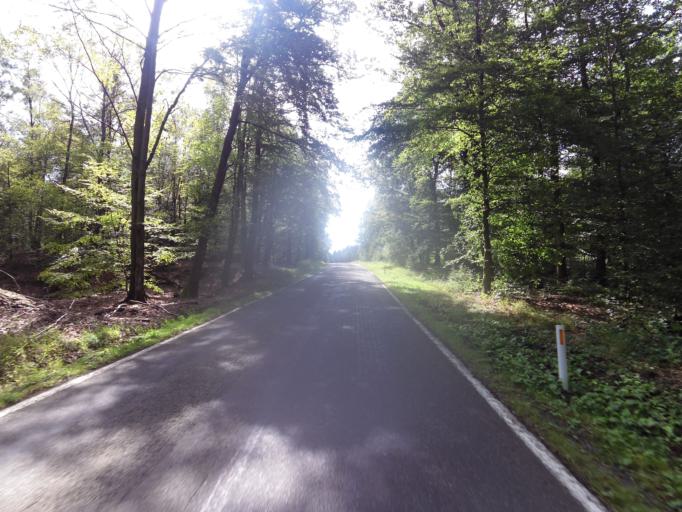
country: BE
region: Wallonia
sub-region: Province du Luxembourg
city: Saint-Hubert
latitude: 50.0579
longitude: 5.3466
